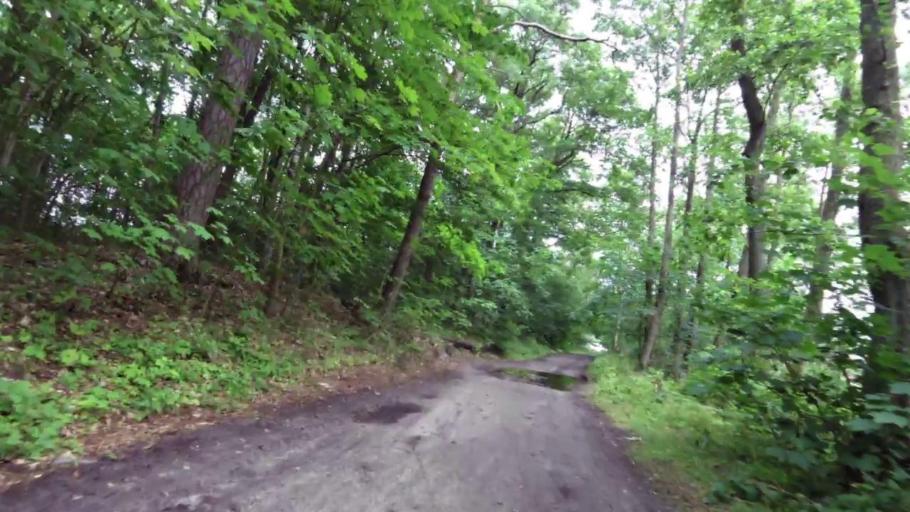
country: PL
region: West Pomeranian Voivodeship
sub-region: Powiat slawienski
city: Darlowo
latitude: 54.5066
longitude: 16.4650
